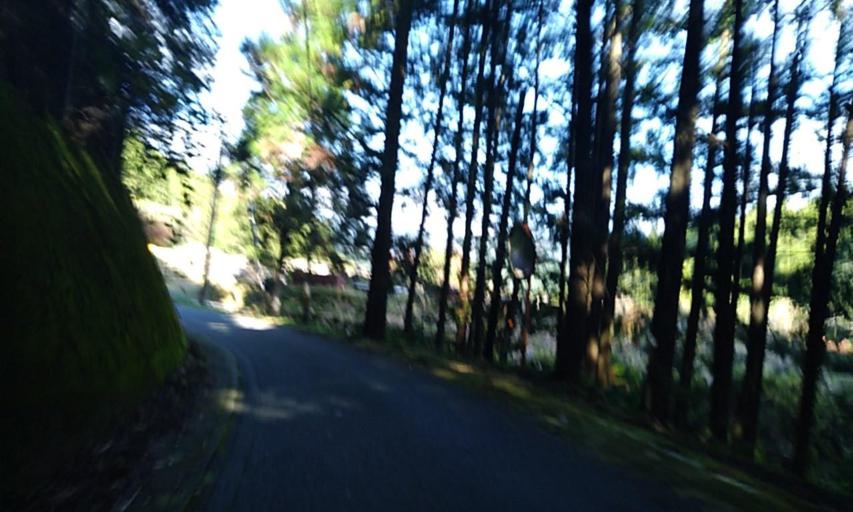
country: JP
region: Wakayama
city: Shingu
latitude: 33.9149
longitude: 135.9903
